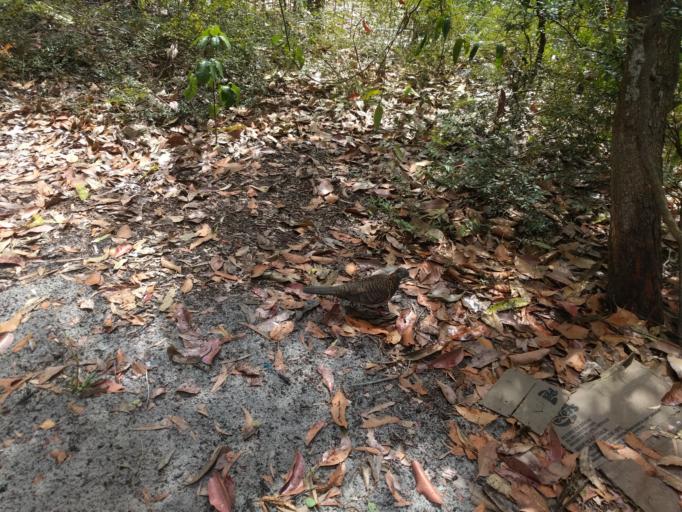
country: AU
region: Queensland
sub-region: Fraser Coast
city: Urangan
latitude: -25.4444
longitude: 153.0508
